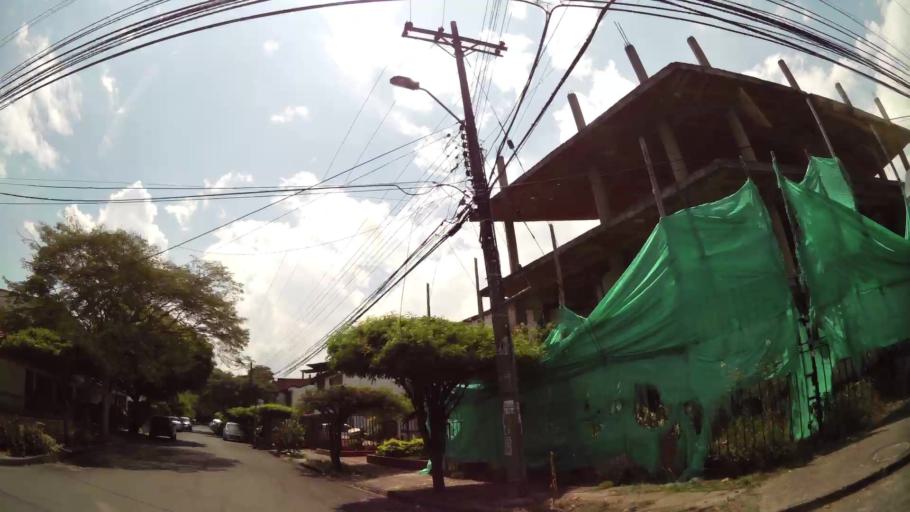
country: CO
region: Valle del Cauca
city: Cali
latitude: 3.4153
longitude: -76.5435
